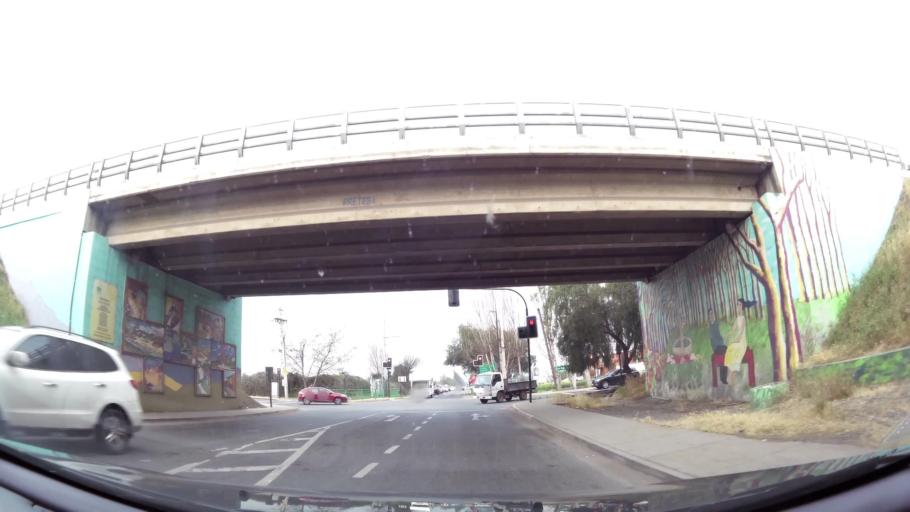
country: CL
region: Santiago Metropolitan
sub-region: Provincia de Chacabuco
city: Chicureo Abajo
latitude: -33.2856
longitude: -70.7017
